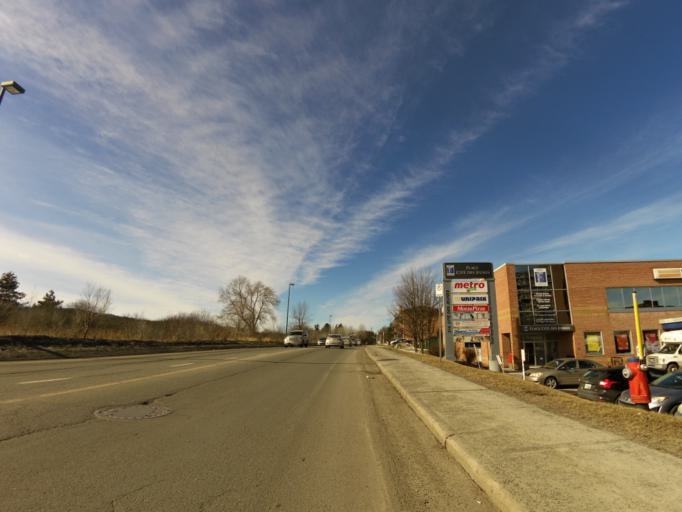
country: CA
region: Quebec
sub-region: Outaouais
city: Gatineau
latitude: 45.4493
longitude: -75.7553
